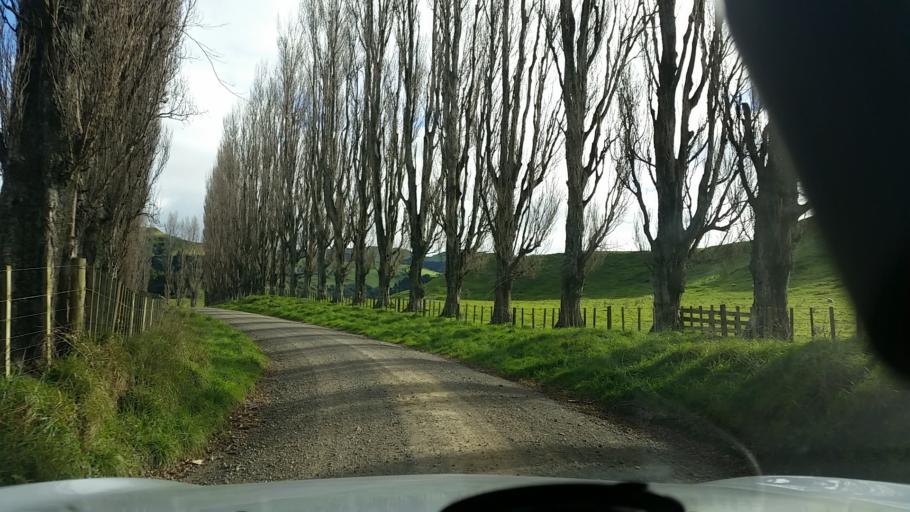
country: NZ
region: Hawke's Bay
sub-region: Napier City
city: Napier
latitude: -39.1016
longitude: 176.8801
